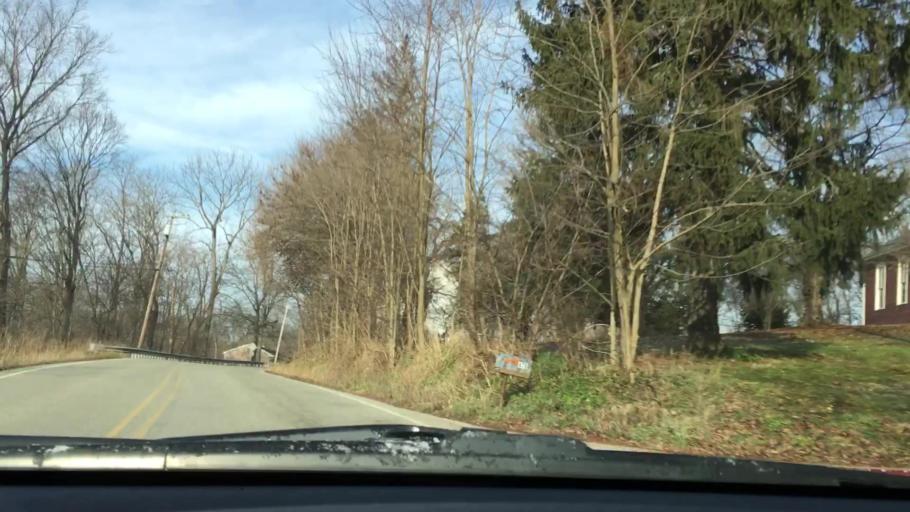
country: US
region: Pennsylvania
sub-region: Westmoreland County
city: Collinsburg
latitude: 40.2607
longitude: -79.7383
